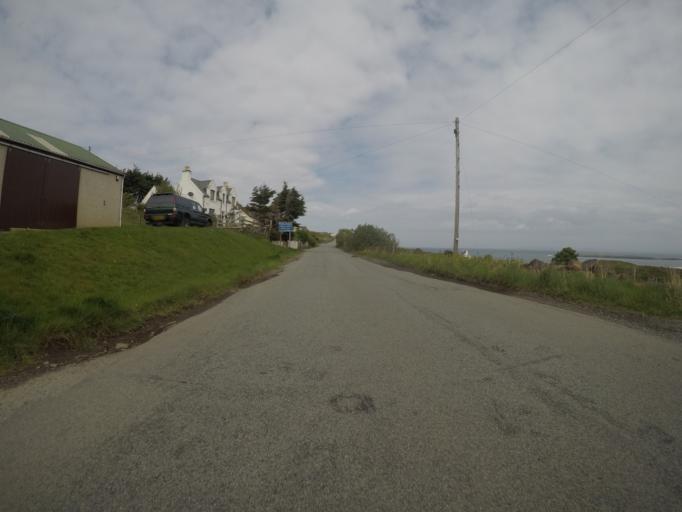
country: GB
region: Scotland
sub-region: Highland
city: Portree
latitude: 57.6333
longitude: -6.2412
